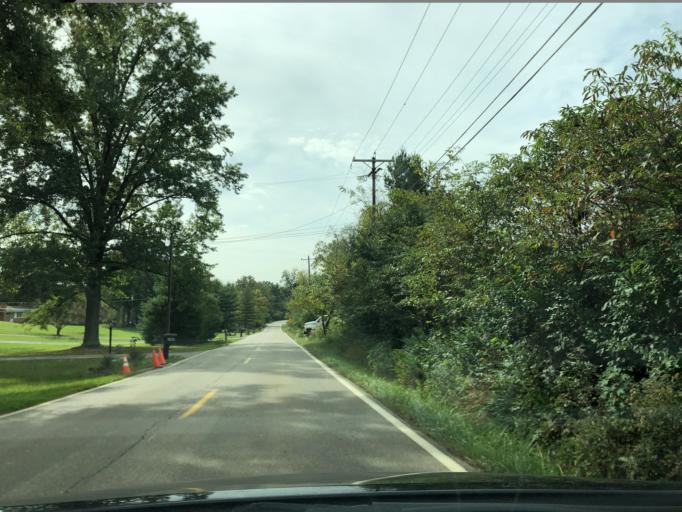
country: US
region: Ohio
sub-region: Hamilton County
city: The Village of Indian Hill
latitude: 39.2377
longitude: -84.2884
